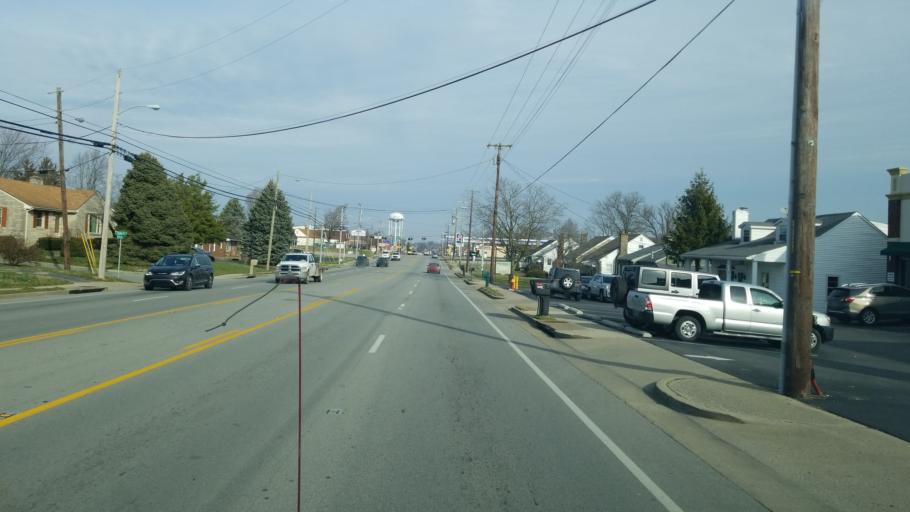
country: US
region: Kentucky
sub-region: Boyle County
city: Danville
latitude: 37.6244
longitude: -84.7746
